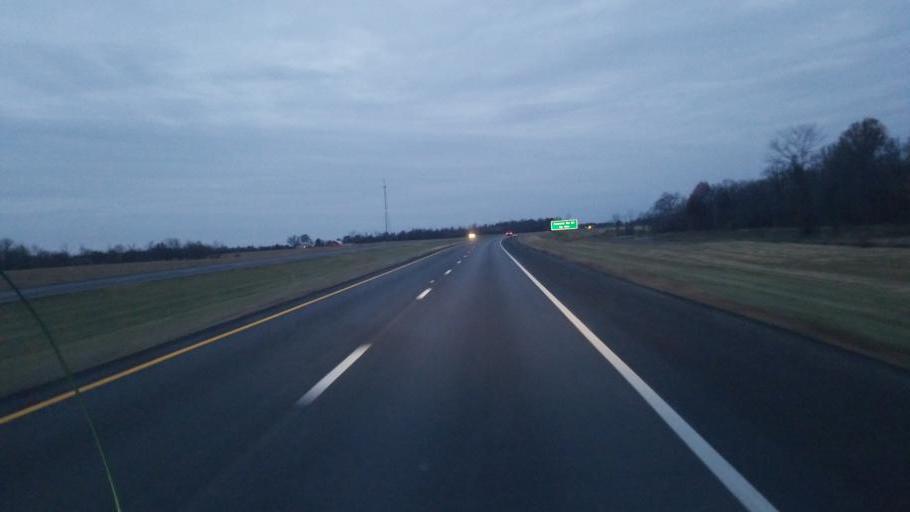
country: US
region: Ohio
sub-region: Hardin County
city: Forest
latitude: 40.8249
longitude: -83.4664
